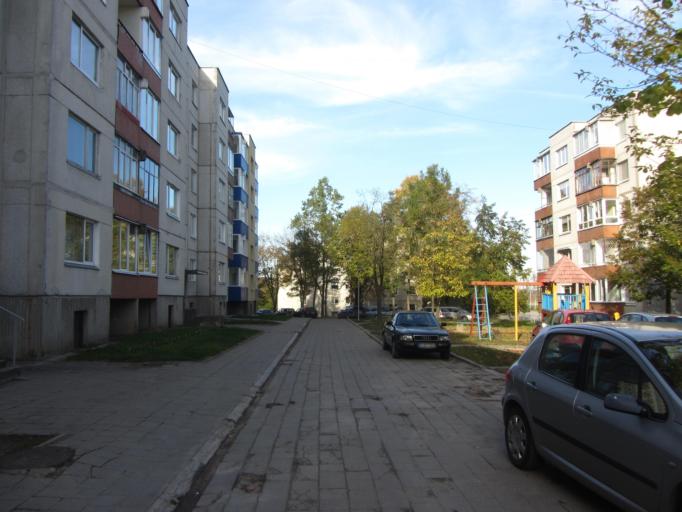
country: LT
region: Vilnius County
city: Elektrenai
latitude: 54.7865
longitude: 24.6695
